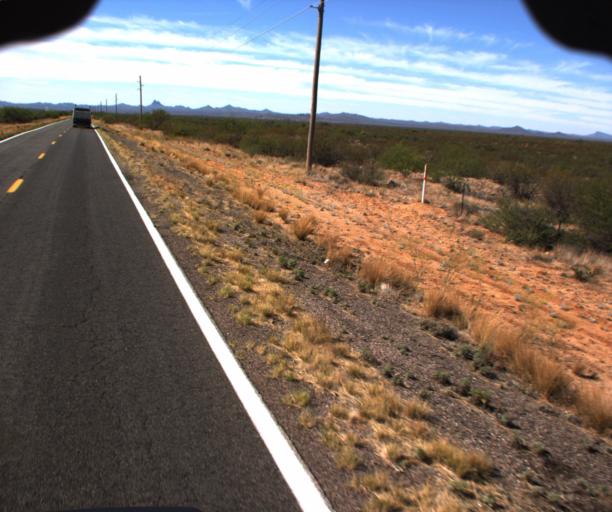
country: US
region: Arizona
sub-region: Yavapai County
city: Congress
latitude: 34.0967
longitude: -112.8291
